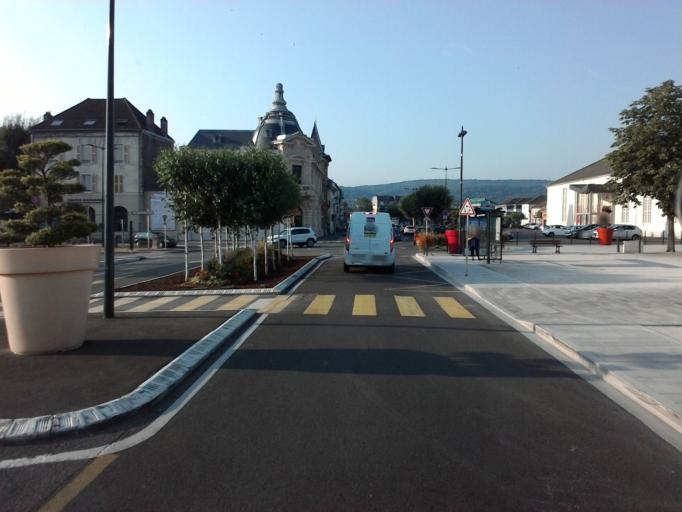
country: FR
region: Franche-Comte
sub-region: Departement de la Haute-Saone
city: Vesoul
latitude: 47.6227
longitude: 6.1600
